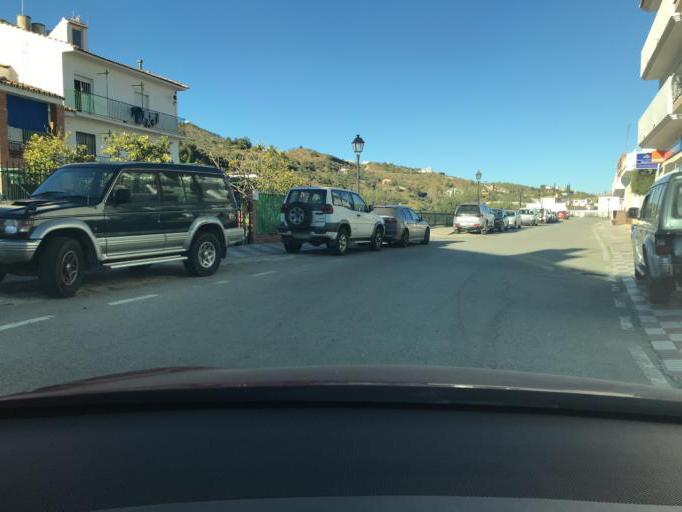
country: ES
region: Andalusia
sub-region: Provincia de Malaga
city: Tolox
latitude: 36.6874
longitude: -4.9020
